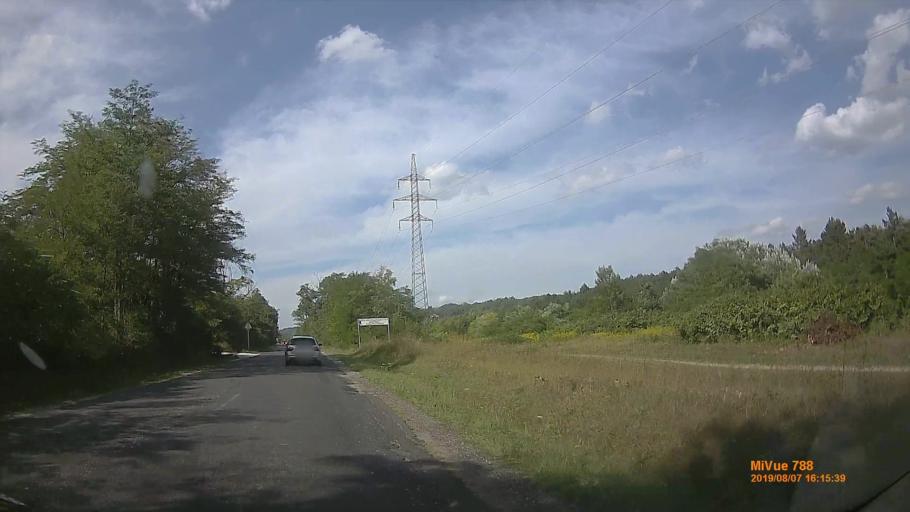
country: HU
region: Zala
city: Gyenesdias
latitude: 46.8031
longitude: 17.2704
